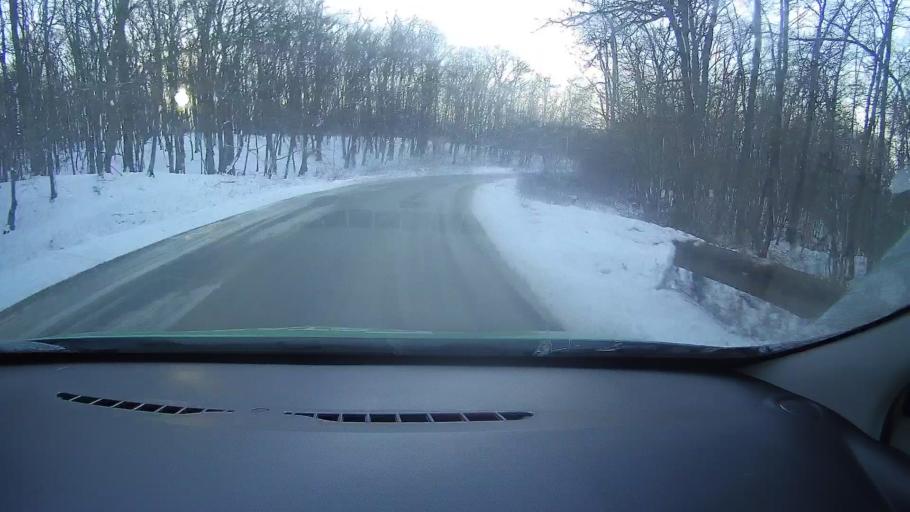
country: RO
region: Sibiu
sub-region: Oras Agnita
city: Ruja
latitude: 45.9870
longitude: 24.6770
